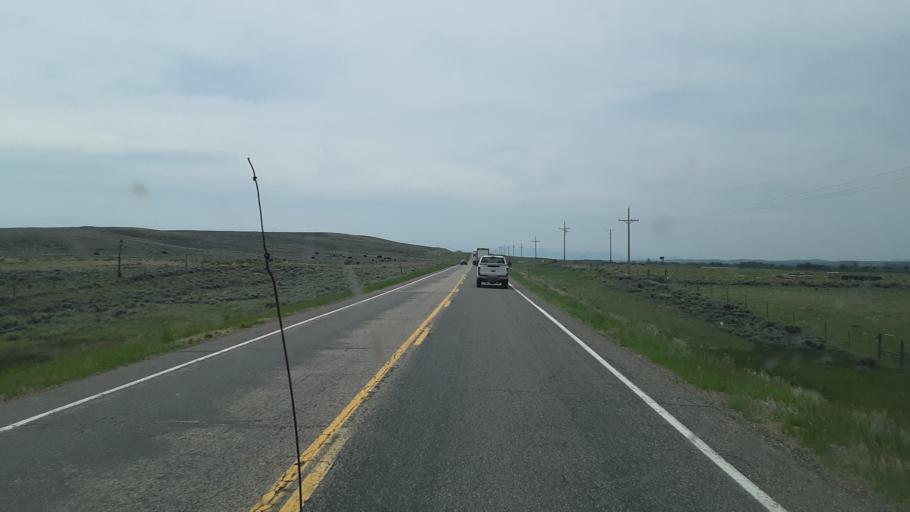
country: US
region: Colorado
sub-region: Jackson County
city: Walden
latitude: 40.7826
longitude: -106.2813
